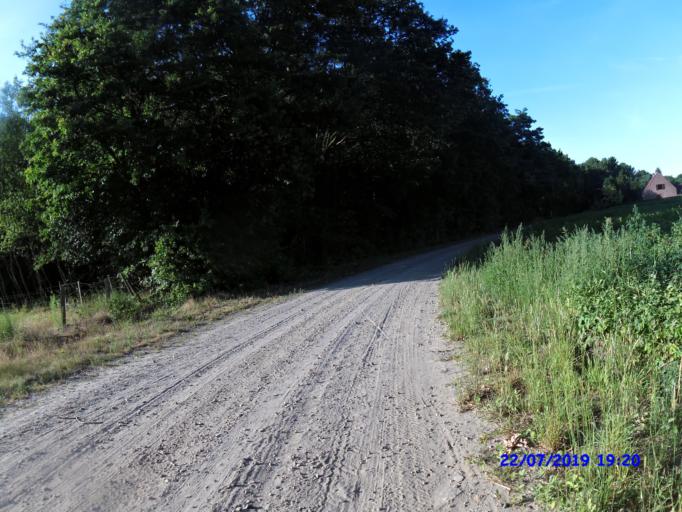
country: BE
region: Flanders
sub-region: Provincie Antwerpen
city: Geel
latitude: 51.1829
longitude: 5.0350
